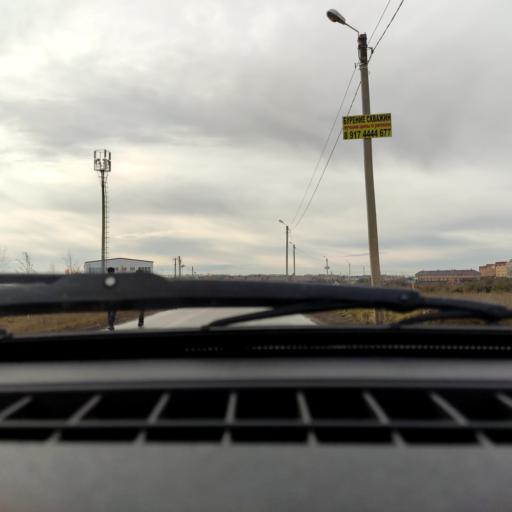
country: RU
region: Bashkortostan
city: Ufa
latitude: 54.6245
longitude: 55.8914
